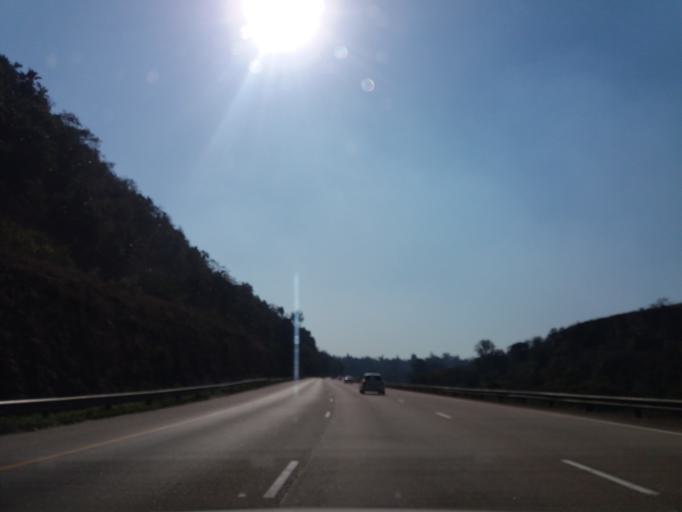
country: ZA
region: KwaZulu-Natal
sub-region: eThekwini Metropolitan Municipality
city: Mpumalanga
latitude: -29.7512
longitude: 30.6647
